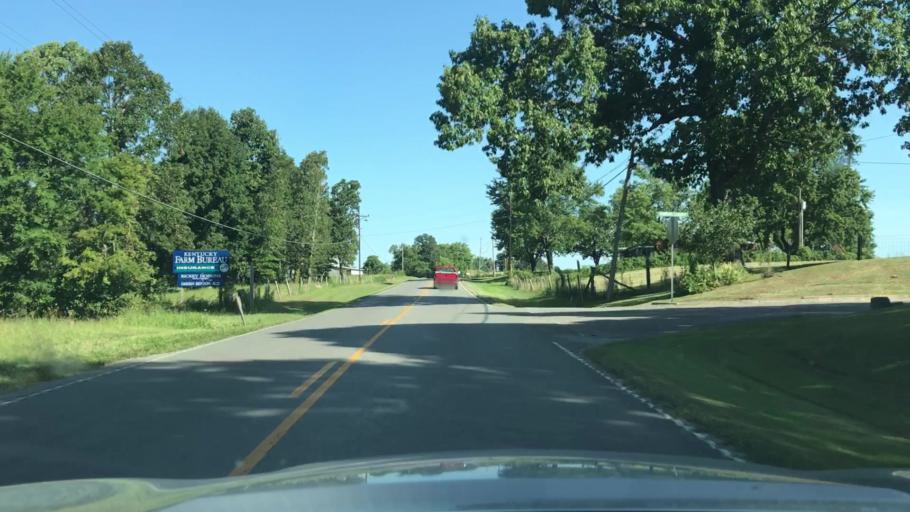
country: US
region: Kentucky
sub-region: Muhlenberg County
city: Greenville
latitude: 37.1702
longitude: -87.1501
